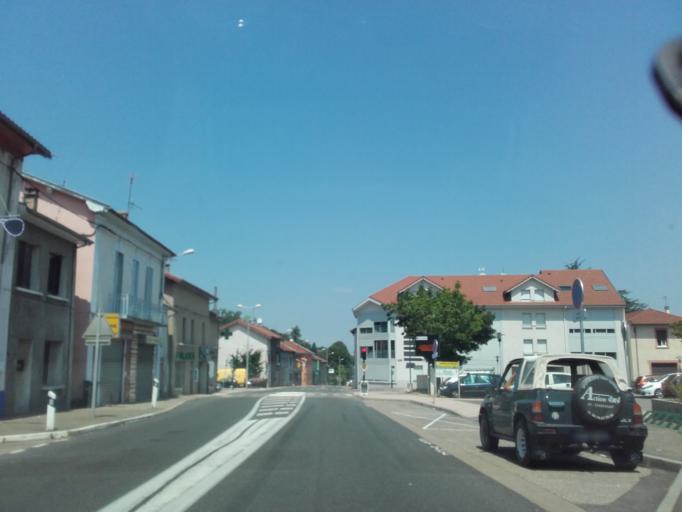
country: FR
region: Rhone-Alpes
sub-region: Departement de l'Isere
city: Nivolas-Vermelle
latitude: 45.5562
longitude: 5.3052
